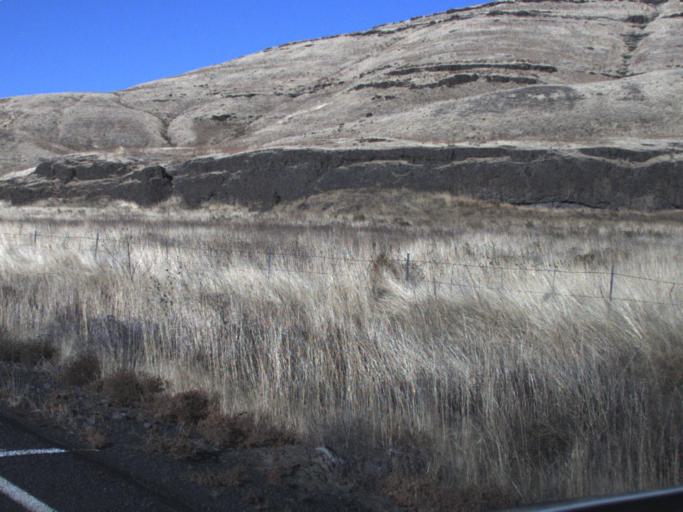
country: US
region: Washington
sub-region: Franklin County
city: Connell
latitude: 46.5771
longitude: -118.5371
